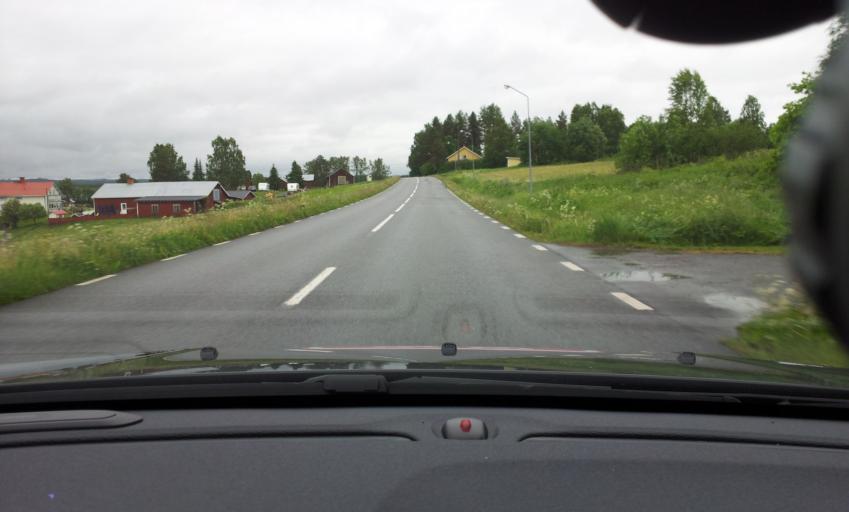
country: SE
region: Jaemtland
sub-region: Stroemsunds Kommun
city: Stroemsund
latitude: 63.5627
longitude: 15.3966
